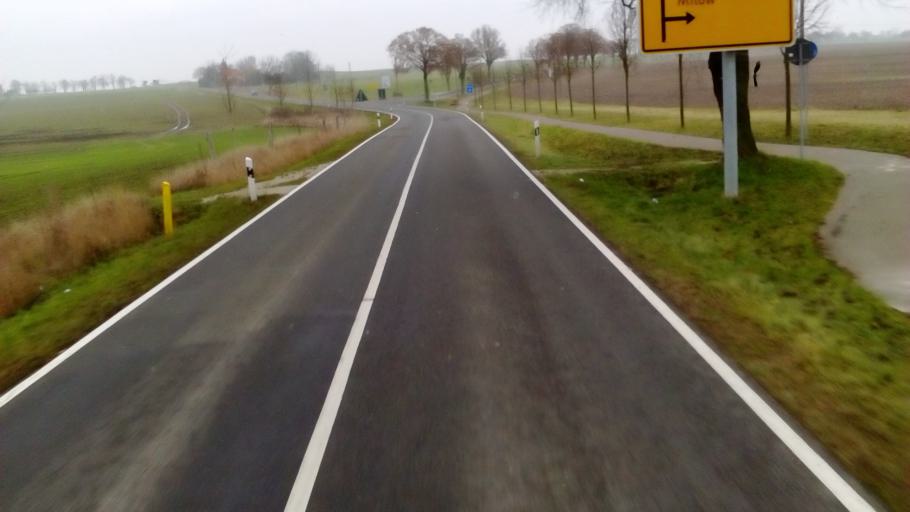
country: DE
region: Mecklenburg-Vorpommern
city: Strasburg
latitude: 53.4913
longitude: 13.8092
